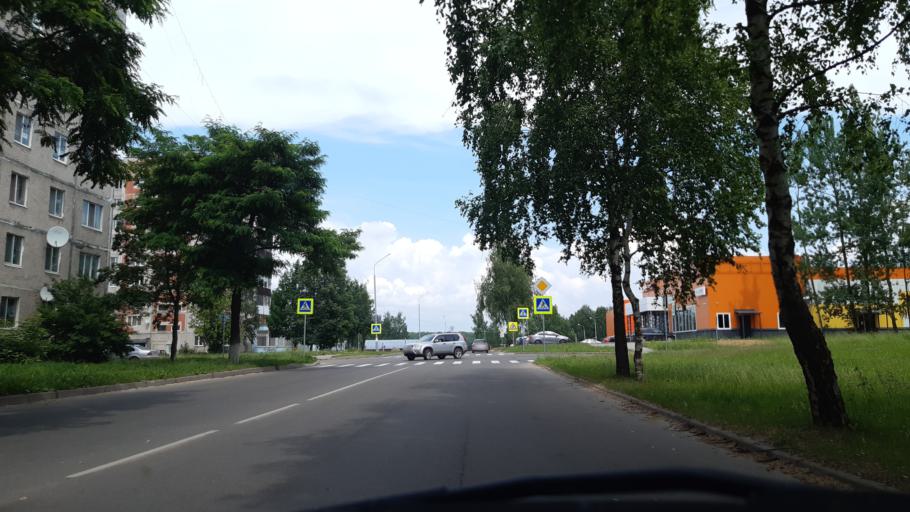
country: RU
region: Smolensk
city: Desnogorsk
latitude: 54.1578
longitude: 33.2919
